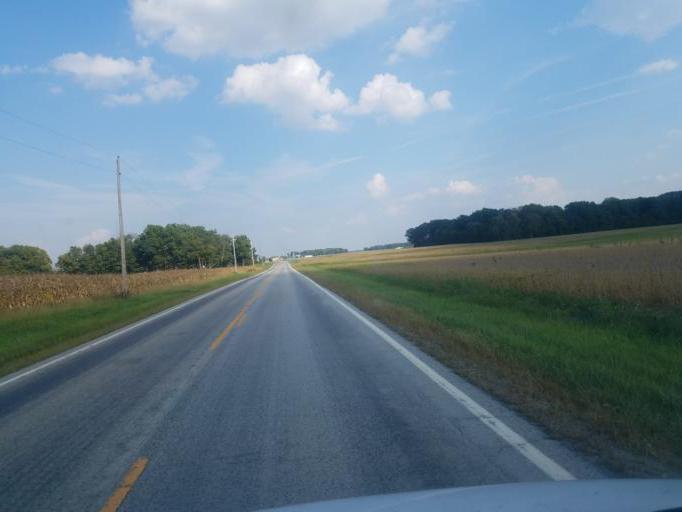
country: US
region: Ohio
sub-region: Hardin County
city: Forest
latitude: 40.8910
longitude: -83.5452
